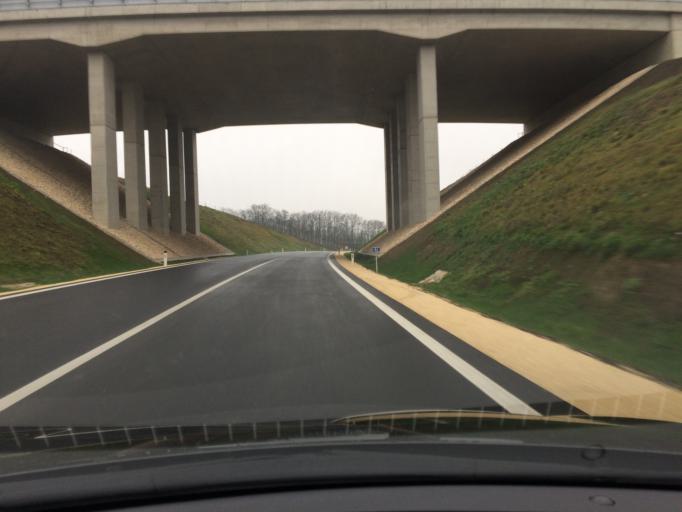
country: AT
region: Lower Austria
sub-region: Politischer Bezirk Mistelbach
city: Mistelbach
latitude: 48.5467
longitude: 16.5785
